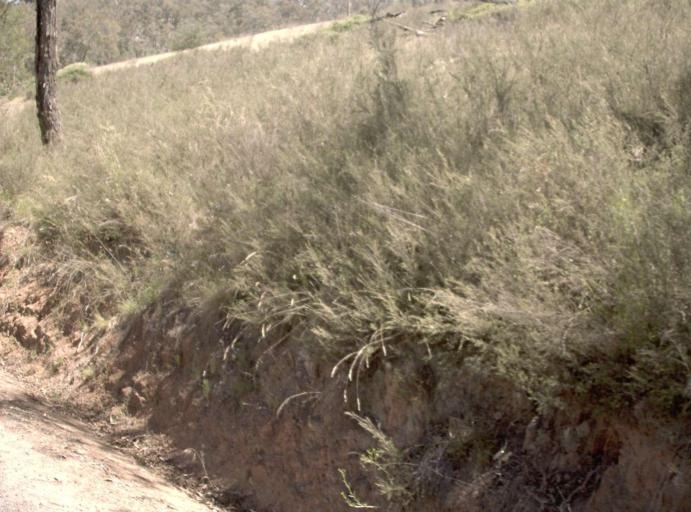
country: AU
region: New South Wales
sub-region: Snowy River
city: Jindabyne
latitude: -37.0574
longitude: 148.5713
